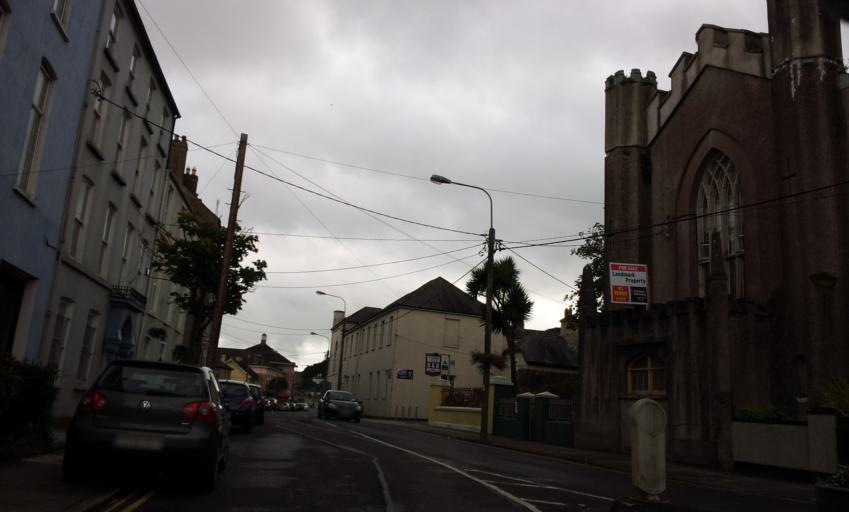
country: IE
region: Munster
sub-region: County Cork
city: Youghal
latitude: 51.9495
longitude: -7.8431
